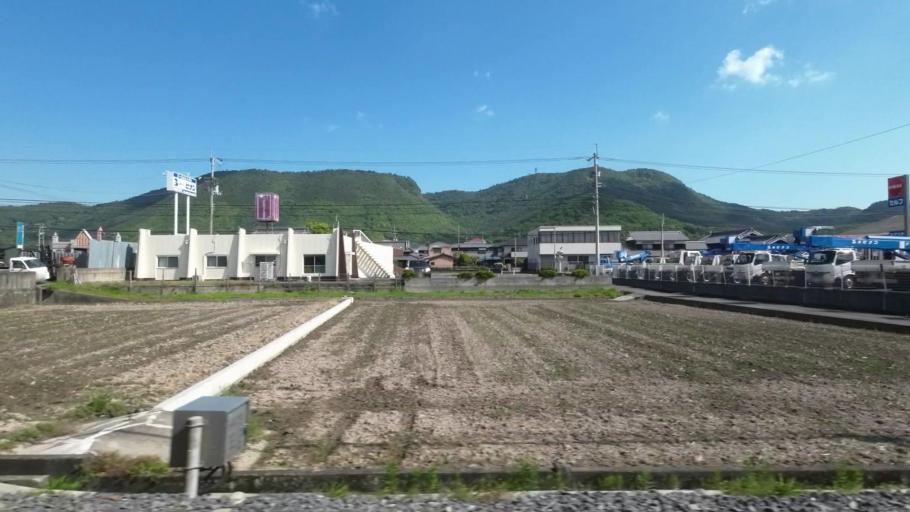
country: JP
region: Kagawa
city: Takamatsu-shi
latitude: 34.3012
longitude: 133.9493
